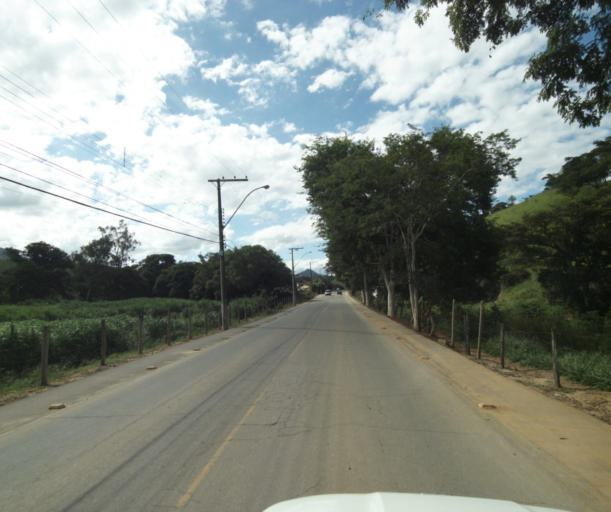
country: BR
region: Espirito Santo
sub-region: Sao Jose Do Calcado
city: Sao Jose do Calcado
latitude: -21.0383
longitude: -41.6526
